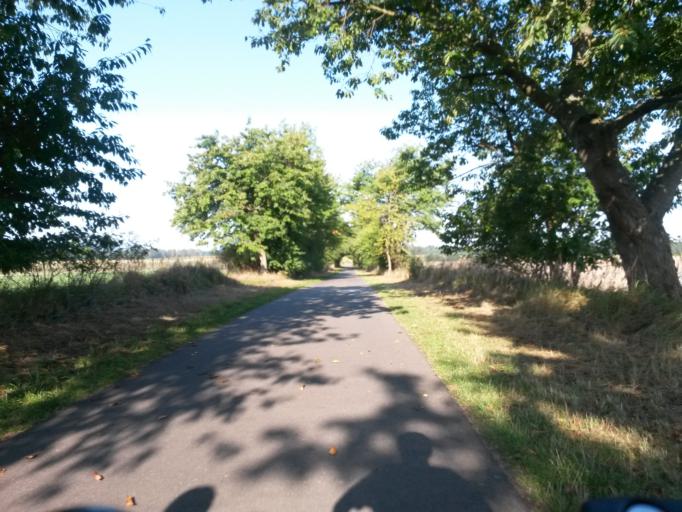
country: DE
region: Brandenburg
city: Templin
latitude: 53.1296
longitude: 13.4676
